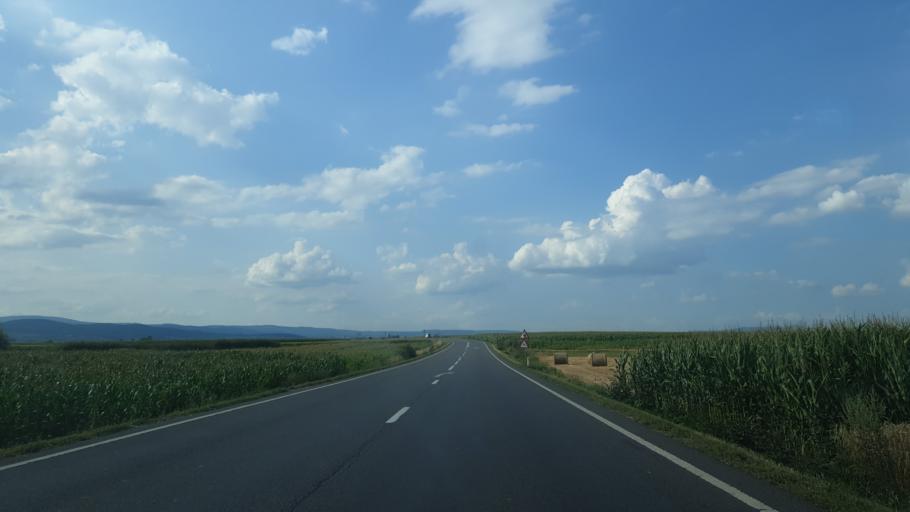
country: RO
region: Covasna
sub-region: Comuna Chichis
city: Chichis
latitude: 45.7894
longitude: 25.8067
